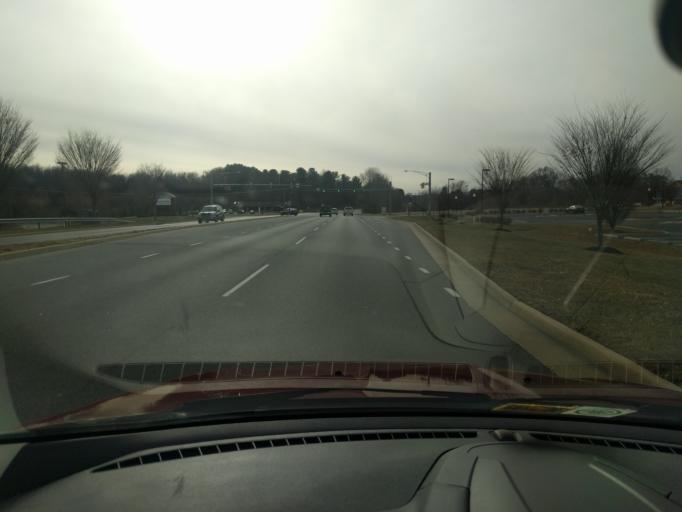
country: US
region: Virginia
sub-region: Augusta County
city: Fishersville
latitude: 38.0758
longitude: -78.9341
